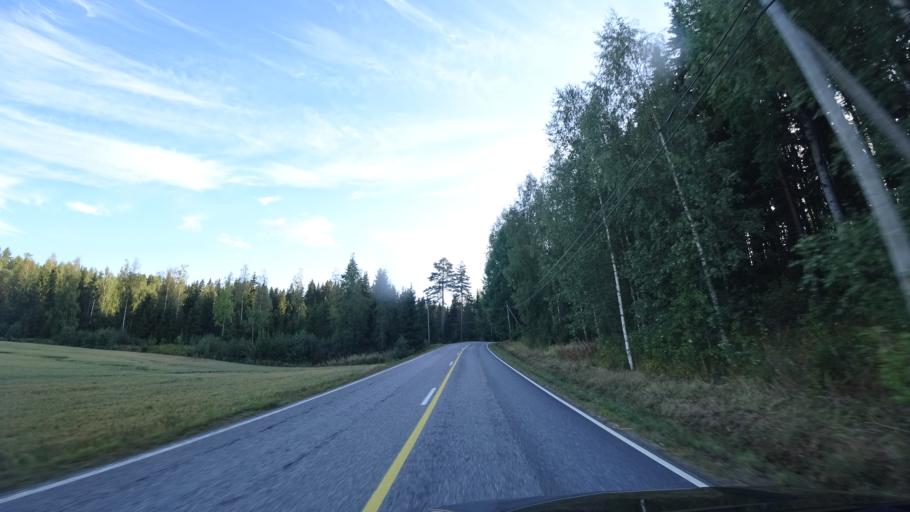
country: FI
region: Haeme
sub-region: Haemeenlinna
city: Lammi
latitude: 61.0156
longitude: 24.9042
